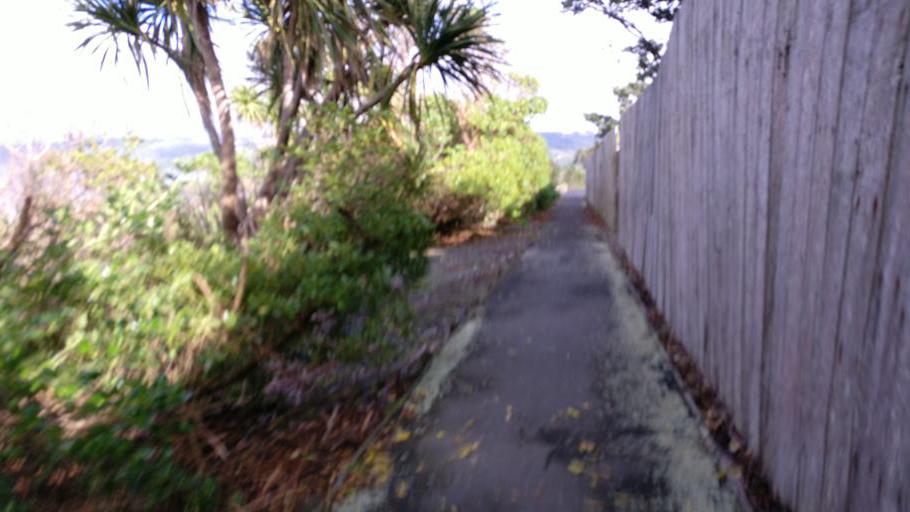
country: NZ
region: Wellington
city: Petone
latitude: -41.2331
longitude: 174.8913
